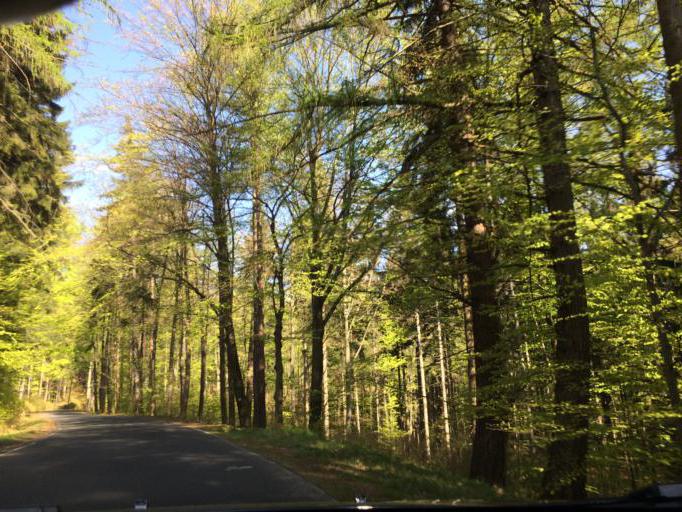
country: PL
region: Lower Silesian Voivodeship
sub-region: Powiat klodzki
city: Jugow
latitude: 50.6693
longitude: 16.5204
